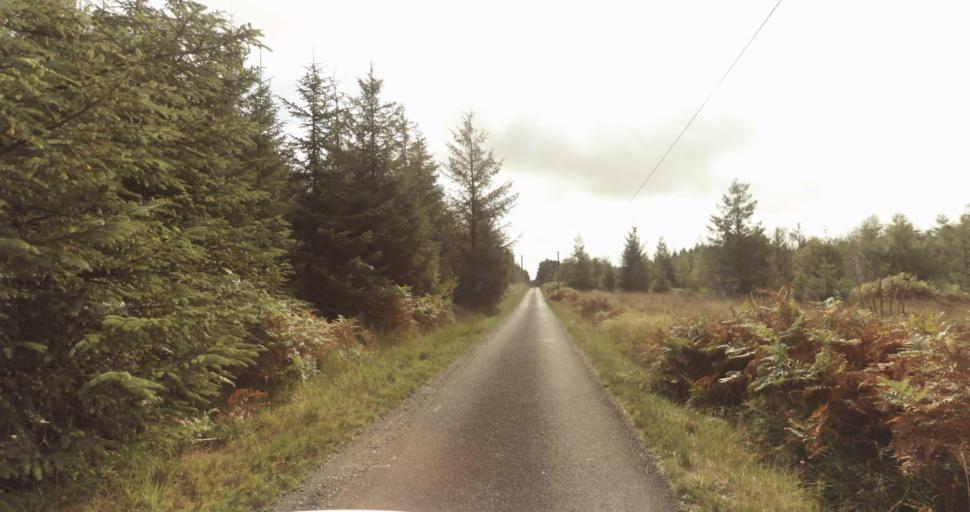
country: FR
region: Lower Normandy
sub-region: Departement de l'Orne
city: Gace
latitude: 48.8397
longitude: 0.3488
